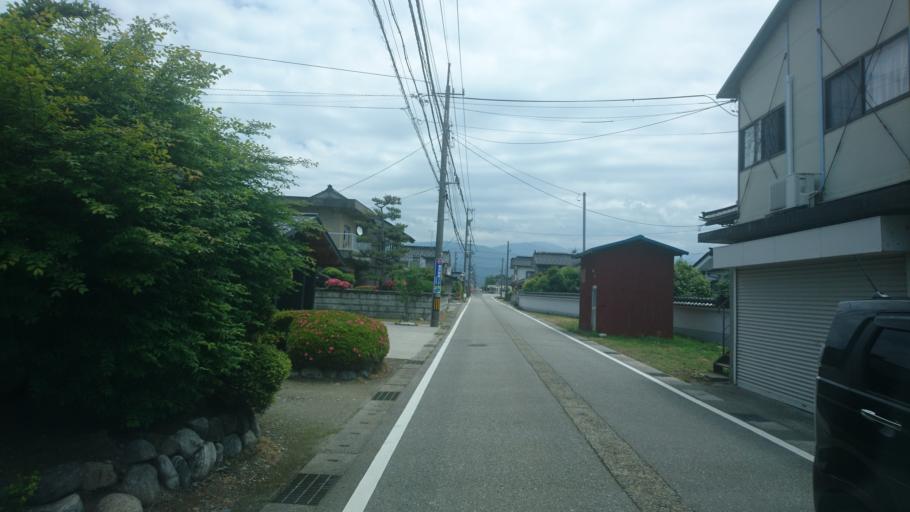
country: JP
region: Toyama
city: Nyuzen
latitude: 36.9391
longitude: 137.5104
